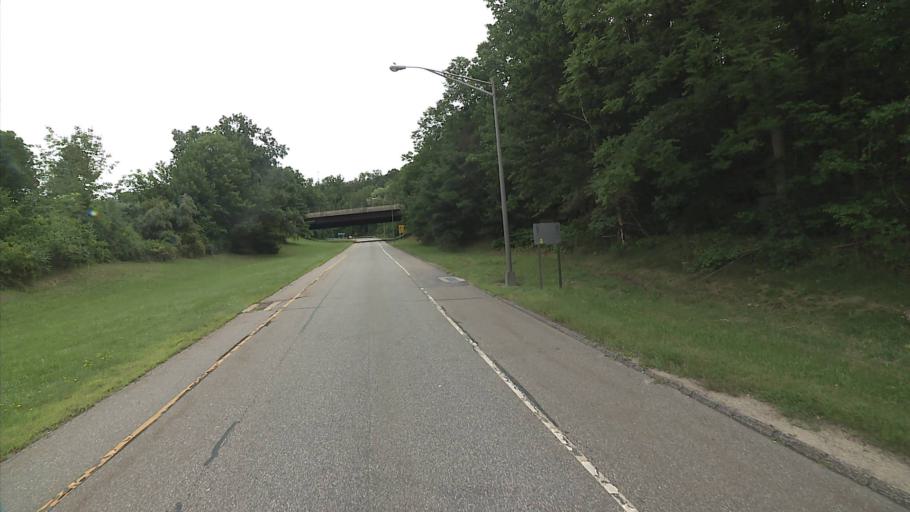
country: US
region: Connecticut
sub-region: Litchfield County
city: Winsted
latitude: 41.9144
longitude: -73.0563
